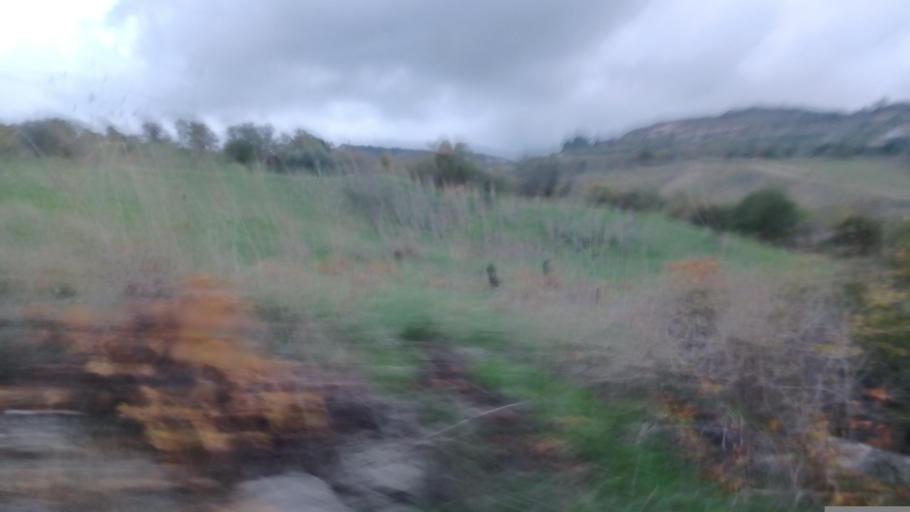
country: CY
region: Pafos
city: Mesogi
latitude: 34.7894
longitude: 32.5300
